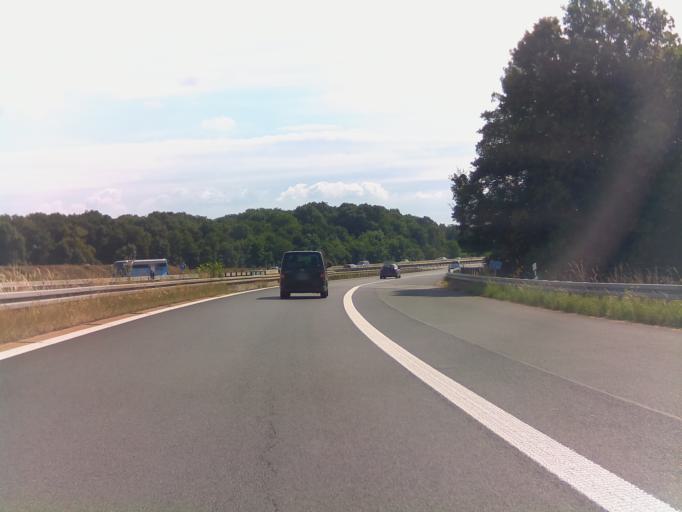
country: DE
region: Bavaria
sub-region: Regierungsbezirk Unterfranken
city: Biebelried
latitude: 49.7782
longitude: 10.0869
